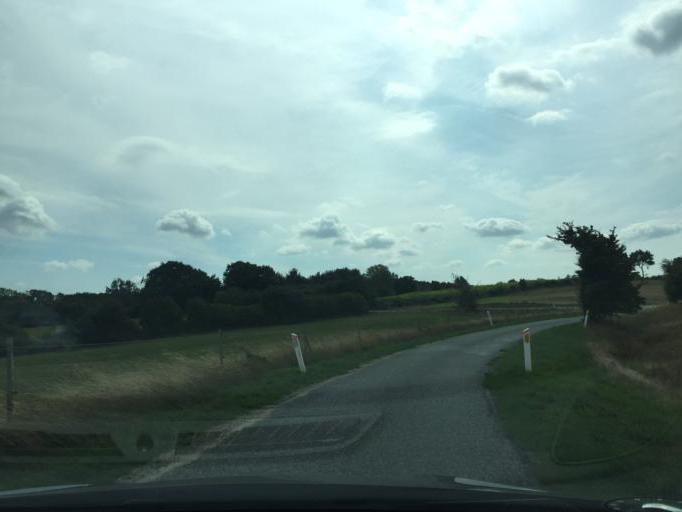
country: DK
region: South Denmark
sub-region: Nordfyns Kommune
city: Sonderso
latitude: 55.4109
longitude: 10.2264
